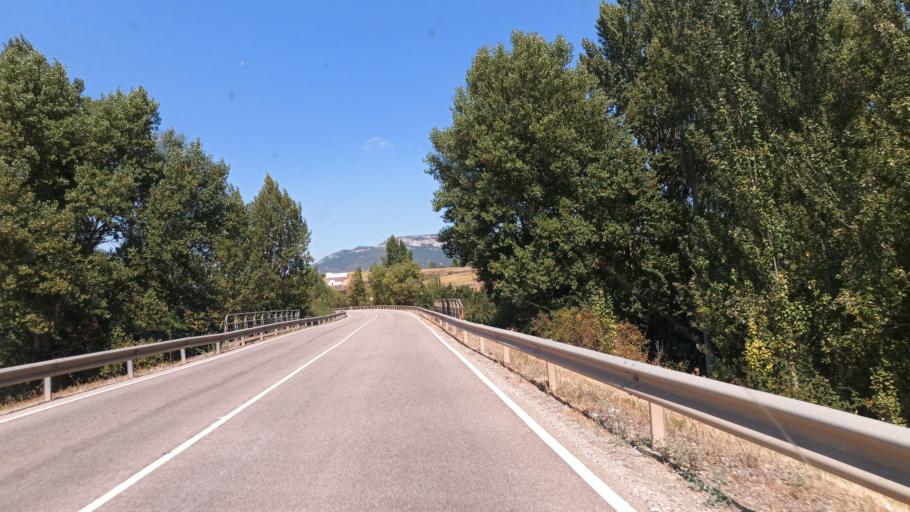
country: ES
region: Castille and Leon
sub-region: Provincia de Burgos
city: Piernigas
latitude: 42.6414
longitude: -3.3869
